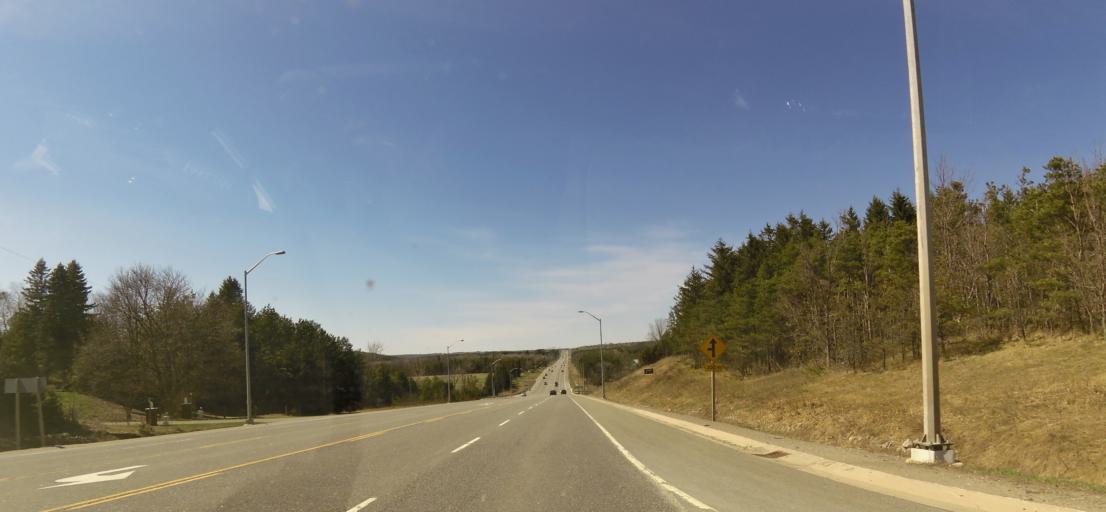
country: CA
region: Ontario
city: Orangeville
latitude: 43.8998
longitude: -80.0496
